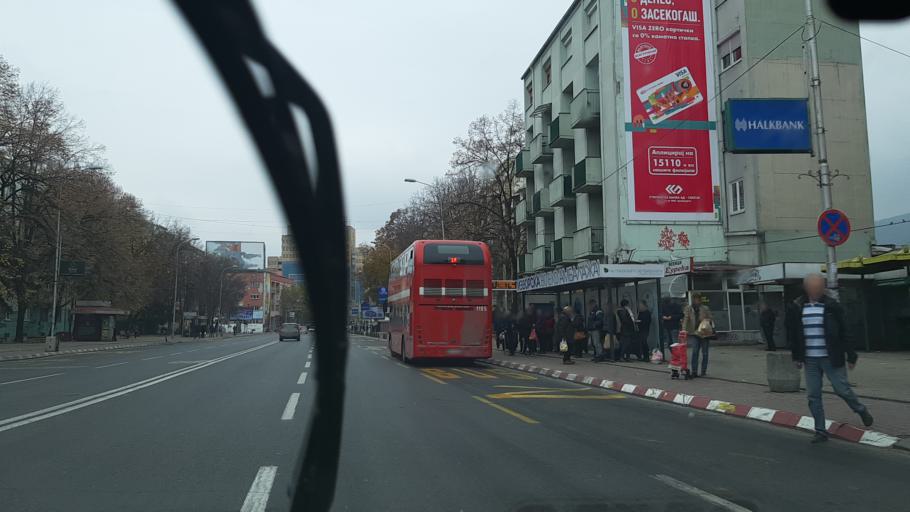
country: MK
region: Karpos
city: Skopje
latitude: 41.9922
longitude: 21.4340
